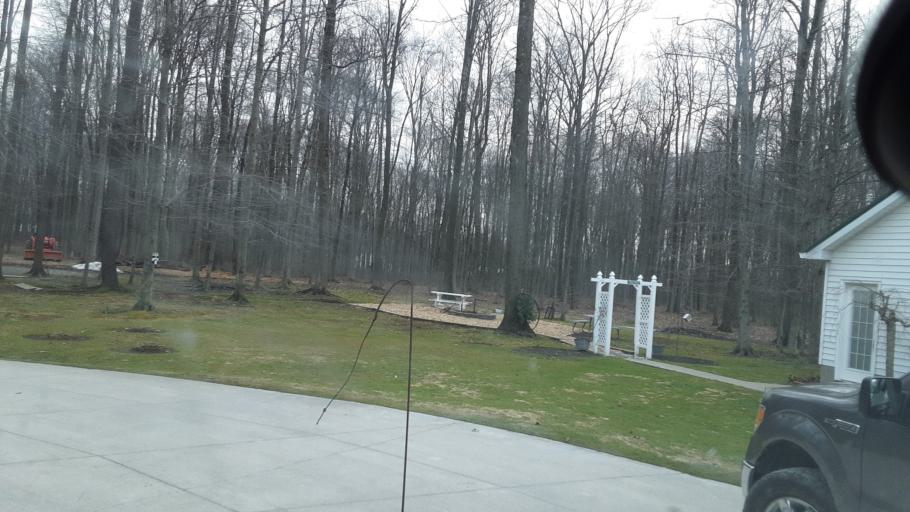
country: US
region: Ohio
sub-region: Geauga County
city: Middlefield
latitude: 41.4040
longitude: -81.0531
